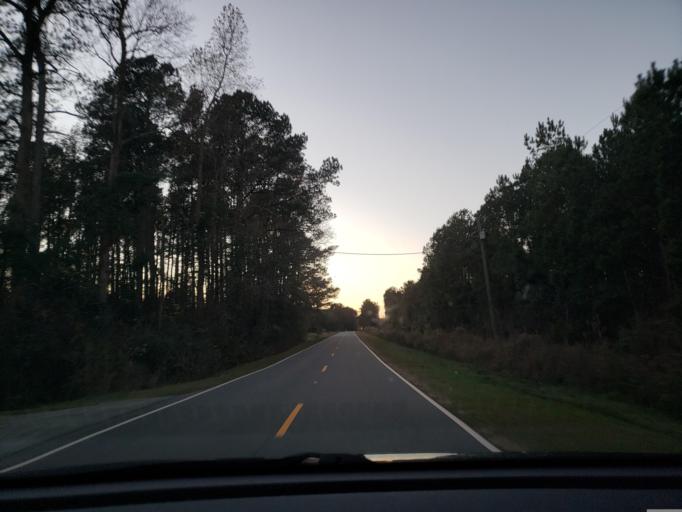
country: US
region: North Carolina
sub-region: Duplin County
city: Beulaville
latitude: 34.7654
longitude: -77.7279
